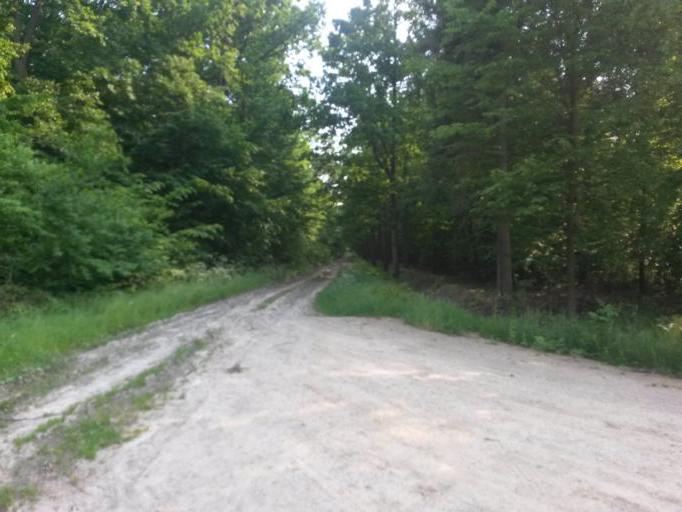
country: PL
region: Lublin Voivodeship
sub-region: Powiat radzynski
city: Borki
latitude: 51.6898
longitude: 22.4804
